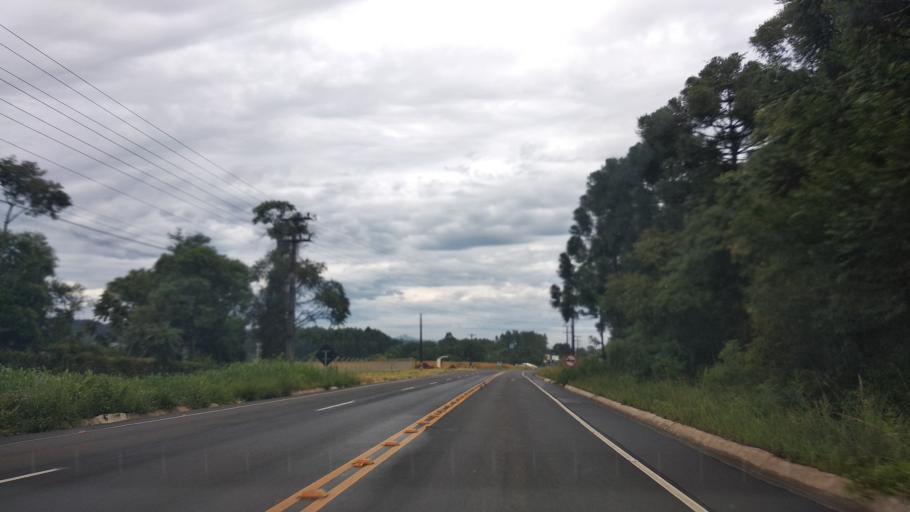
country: BR
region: Santa Catarina
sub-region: Videira
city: Videira
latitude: -27.0527
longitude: -51.1854
